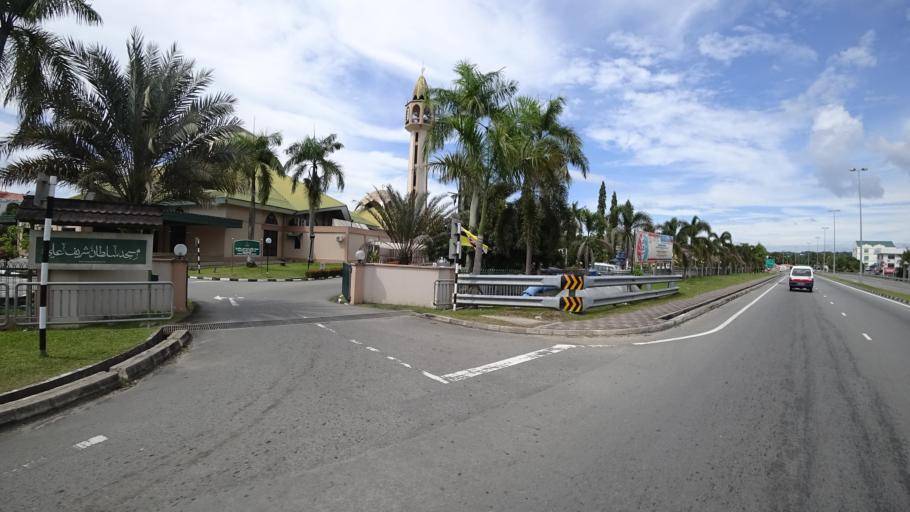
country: BN
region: Brunei and Muara
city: Bandar Seri Begawan
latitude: 4.8877
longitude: 114.8421
